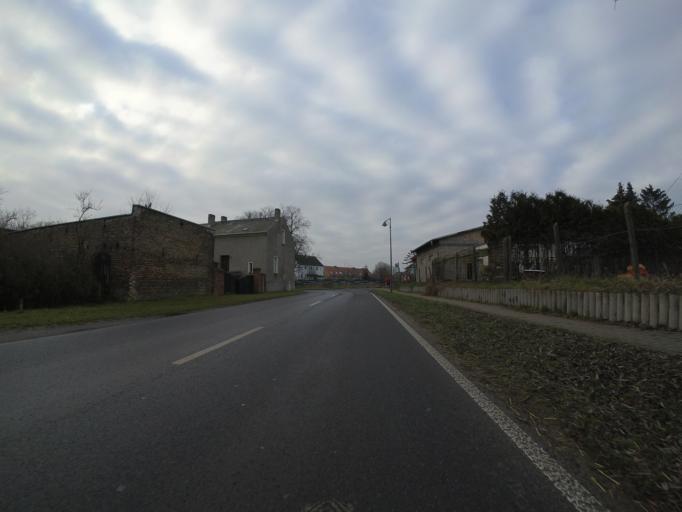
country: DE
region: Berlin
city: Hellersdorf
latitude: 52.5690
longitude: 13.6214
